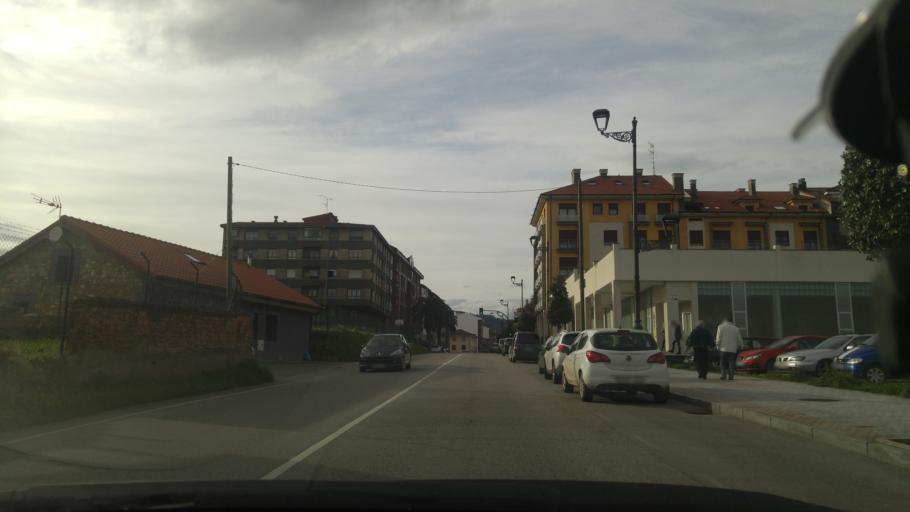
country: ES
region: Asturias
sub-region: Province of Asturias
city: Llanera
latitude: 43.4380
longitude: -5.8492
